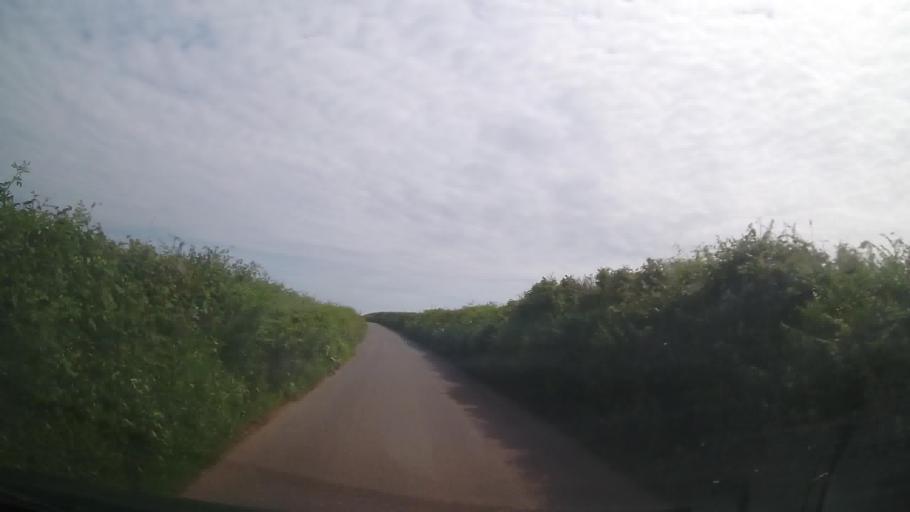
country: GB
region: England
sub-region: Devon
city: Salcombe
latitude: 50.2477
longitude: -3.6823
